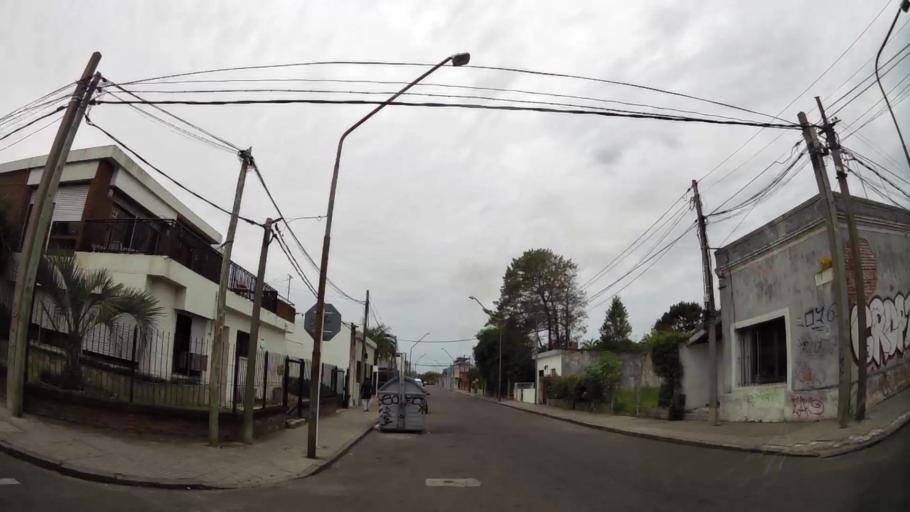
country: UY
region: Maldonado
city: Maldonado
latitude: -34.9118
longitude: -54.9554
